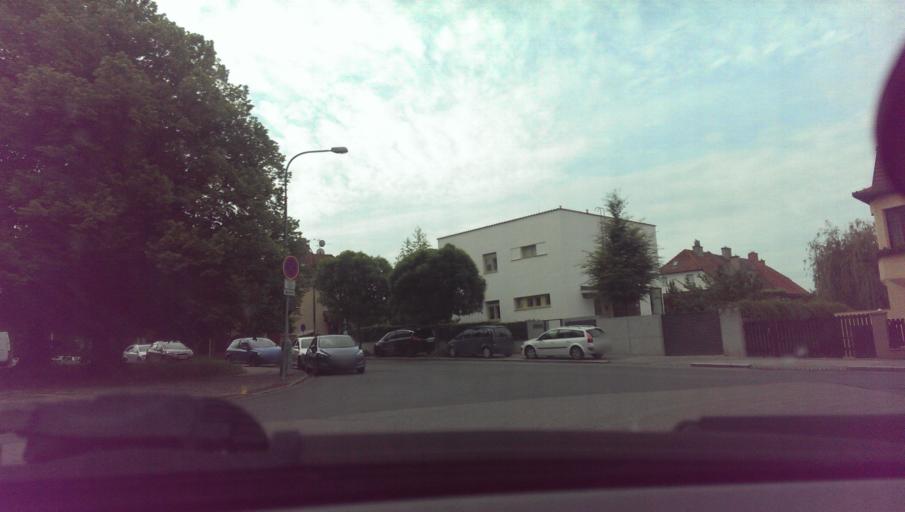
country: CZ
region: South Moravian
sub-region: Mesto Brno
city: Brno
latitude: 49.2089
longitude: 16.6144
